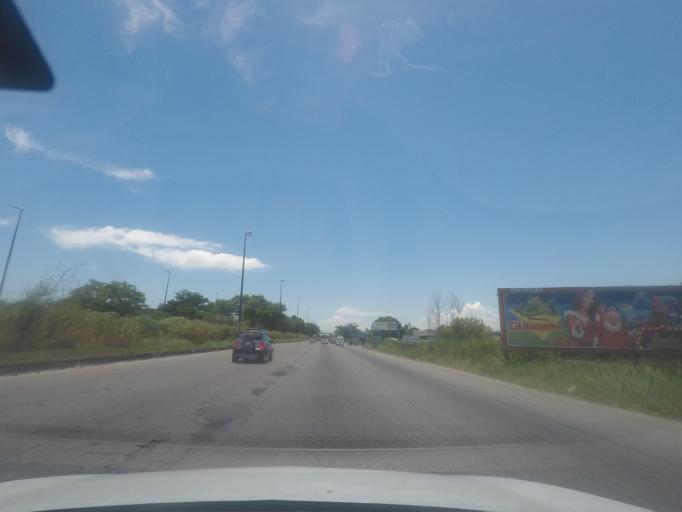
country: BR
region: Rio de Janeiro
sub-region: Itaguai
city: Itaguai
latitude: -22.8906
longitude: -43.6659
